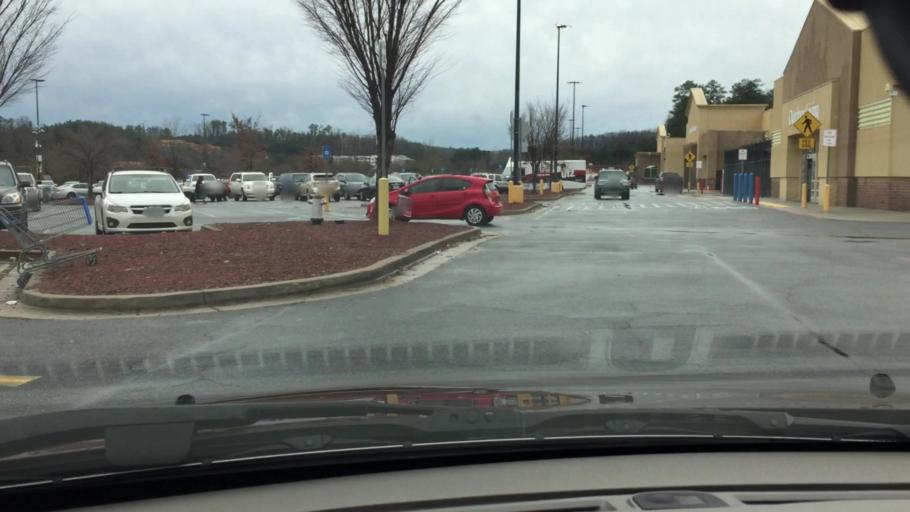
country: US
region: Georgia
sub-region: Cobb County
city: Kennesaw
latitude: 34.0206
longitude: -84.5563
